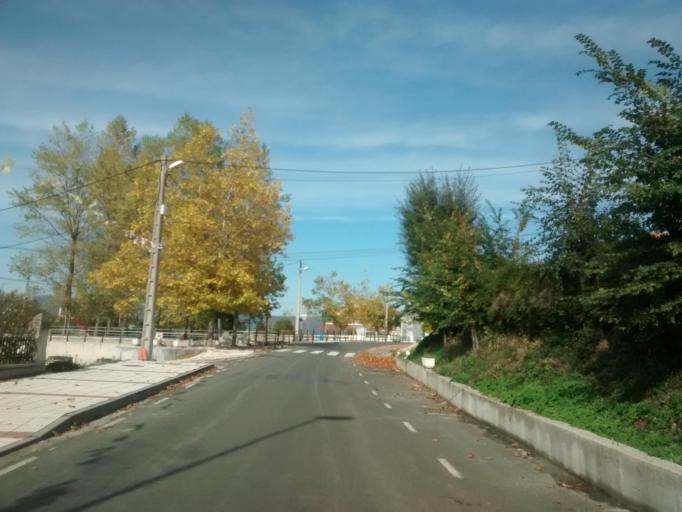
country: ES
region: Castille and Leon
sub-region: Provincia de Burgos
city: Arija
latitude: 42.9857
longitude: -3.9598
